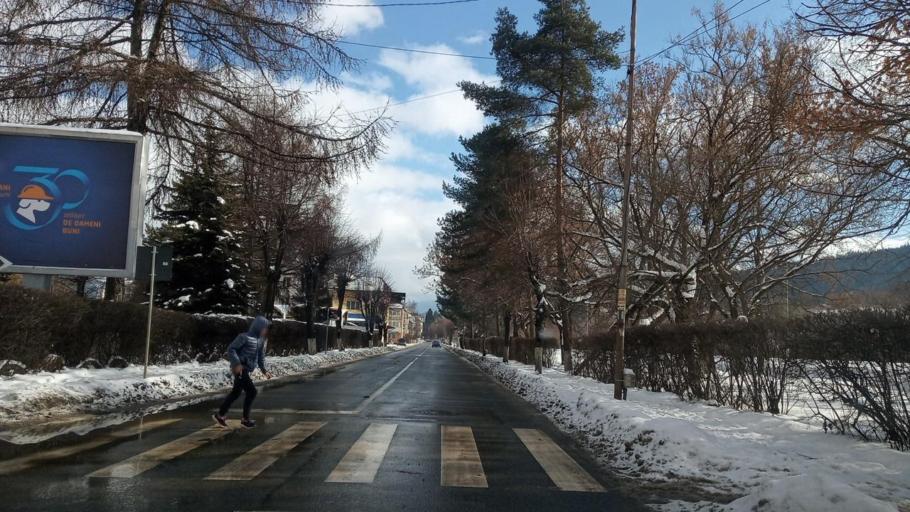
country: RO
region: Suceava
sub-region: Municipiul Vatra Dornei
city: Vatra Dornei
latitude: 47.3471
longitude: 25.3488
